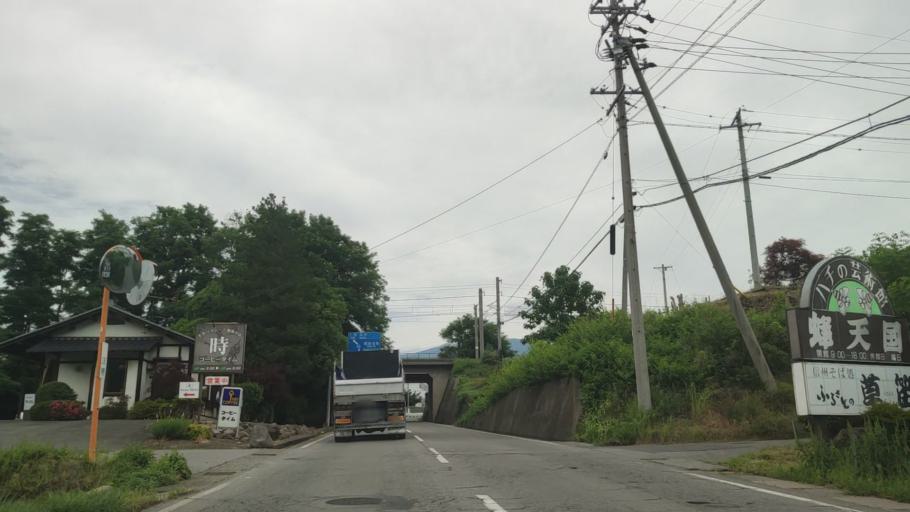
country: JP
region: Nagano
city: Kamimaruko
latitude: 36.3430
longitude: 138.3521
